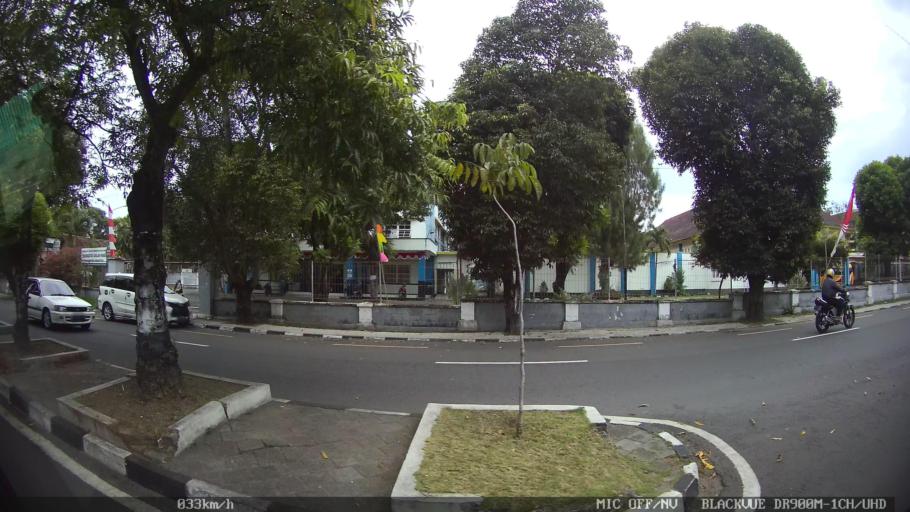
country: ID
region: Daerah Istimewa Yogyakarta
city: Yogyakarta
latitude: -7.7952
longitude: 110.3832
